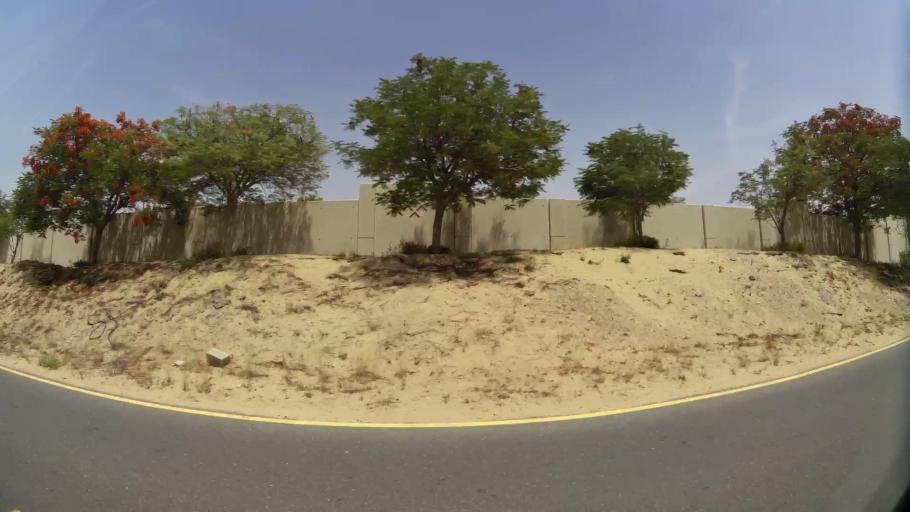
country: AE
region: Ash Shariqah
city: Sharjah
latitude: 25.2354
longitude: 55.4893
